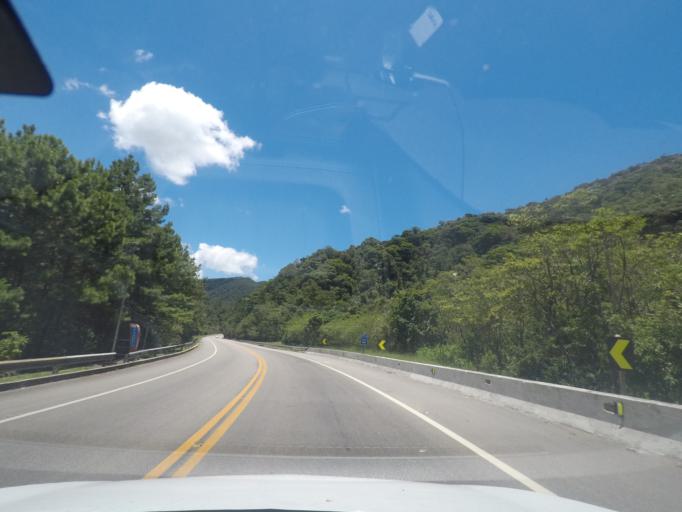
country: BR
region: Rio de Janeiro
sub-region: Teresopolis
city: Teresopolis
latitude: -22.4594
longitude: -42.9731
